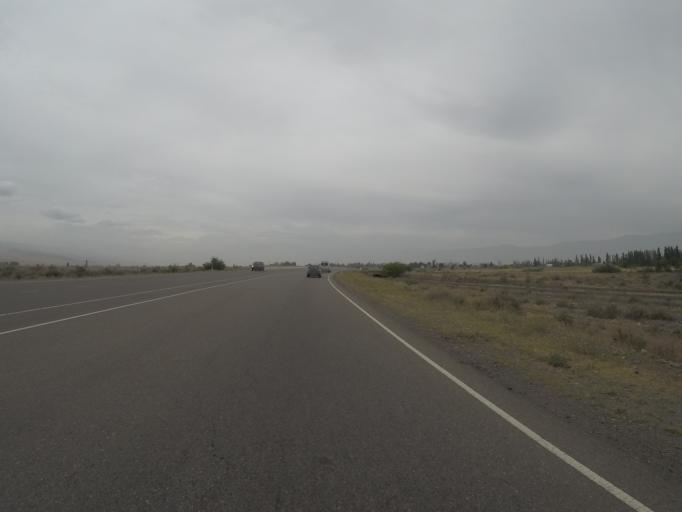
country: KG
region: Chuy
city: Bystrovka
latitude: 42.8283
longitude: 75.5380
